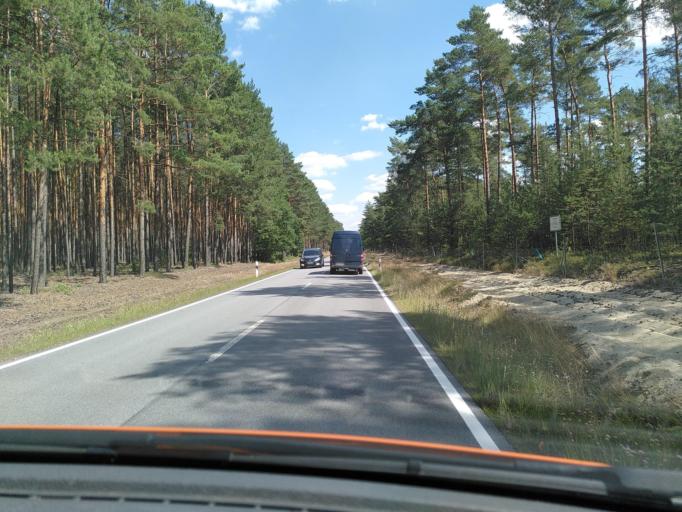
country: PL
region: Lubusz
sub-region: Powiat zarski
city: Przewoz
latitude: 51.4803
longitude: 14.8852
